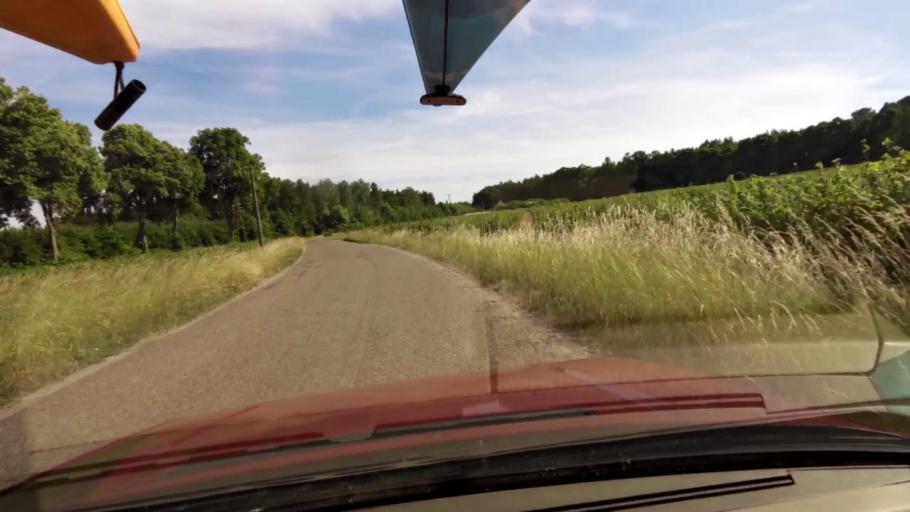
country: PL
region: Pomeranian Voivodeship
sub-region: Powiat slupski
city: Kepice
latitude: 54.1727
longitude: 16.8868
